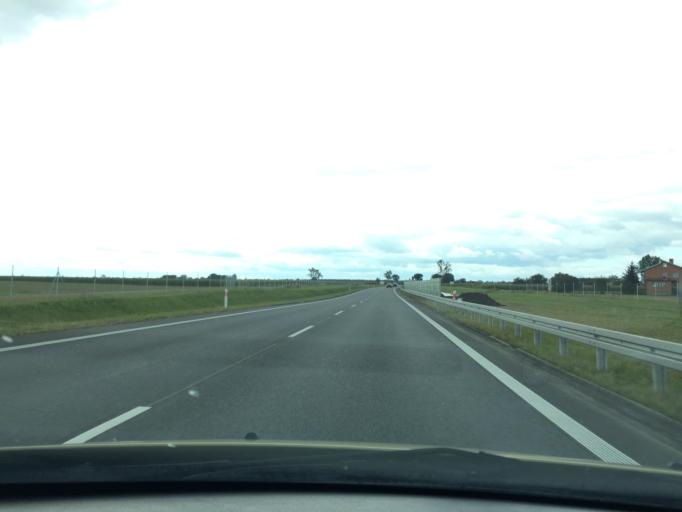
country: PL
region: Greater Poland Voivodeship
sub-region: Powiat sredzki
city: Nowe Miasto nad Warta
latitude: 52.0475
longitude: 17.4414
